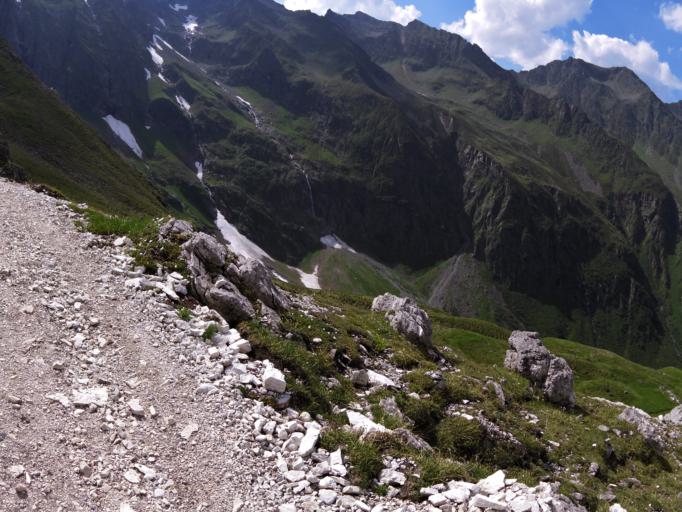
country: AT
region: Tyrol
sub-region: Politischer Bezirk Innsbruck Land
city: Gschnitz
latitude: 47.0501
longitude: 11.3147
